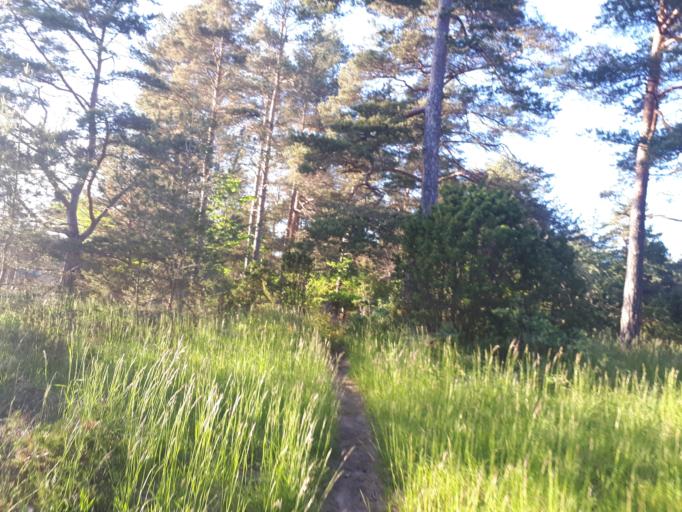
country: SE
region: Gotland
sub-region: Gotland
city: Visby
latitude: 57.6056
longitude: 18.2895
